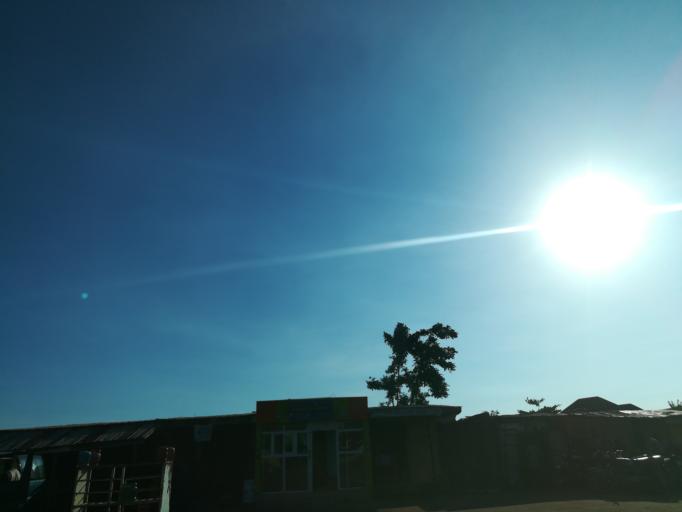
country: NG
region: Lagos
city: Ikorodu
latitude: 6.5745
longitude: 3.5283
